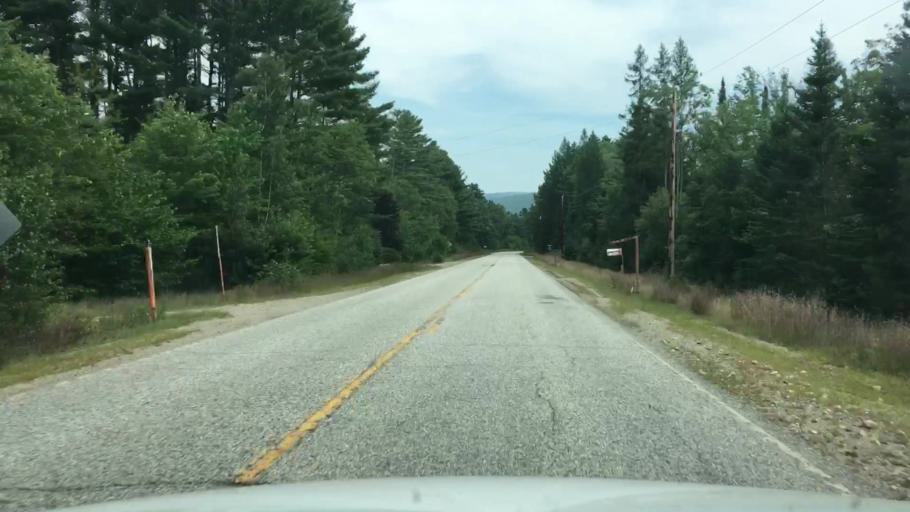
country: US
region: Maine
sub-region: Oxford County
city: Rumford
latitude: 44.6155
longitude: -70.7417
